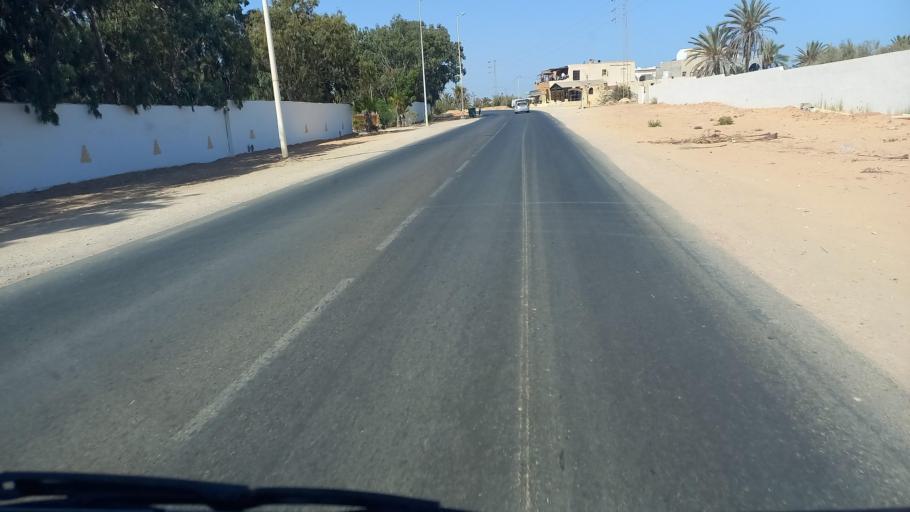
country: TN
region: Madanin
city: Midoun
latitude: 33.7809
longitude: 11.0447
